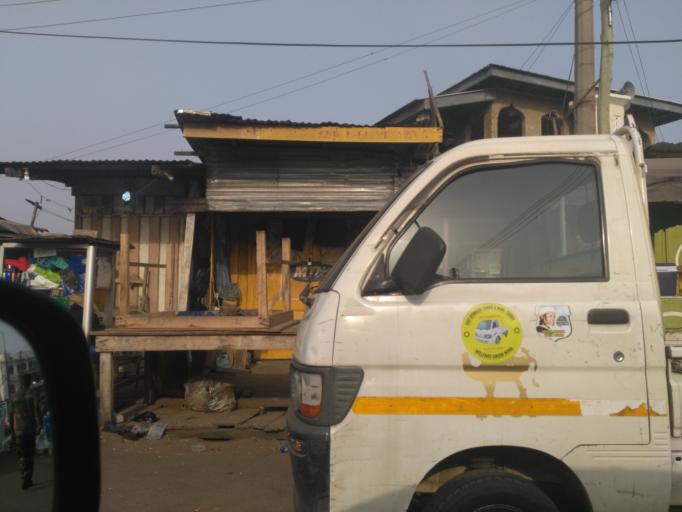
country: GH
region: Greater Accra
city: Accra
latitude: 5.5803
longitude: -0.1995
